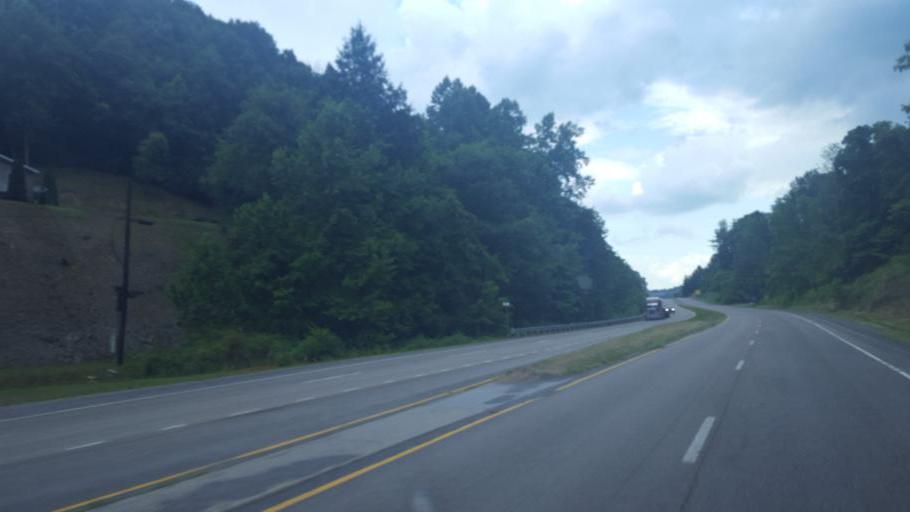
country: US
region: Virginia
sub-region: Wise County
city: Pound
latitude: 37.1346
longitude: -82.6233
